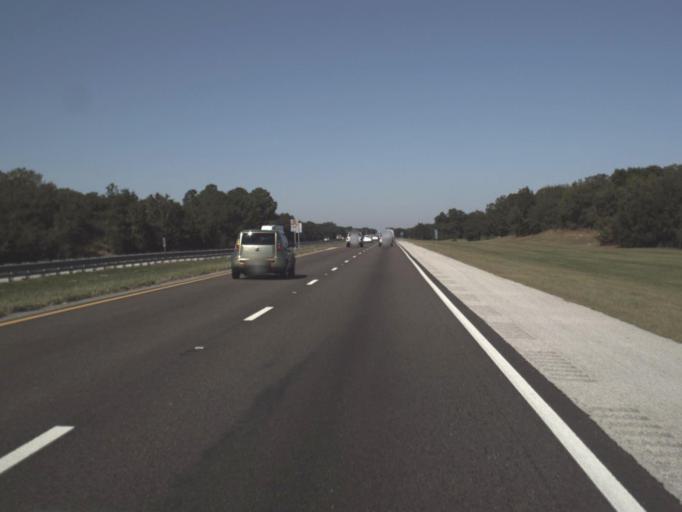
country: US
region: Florida
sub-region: Lake County
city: Hawthorne
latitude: 28.7182
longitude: -81.8993
